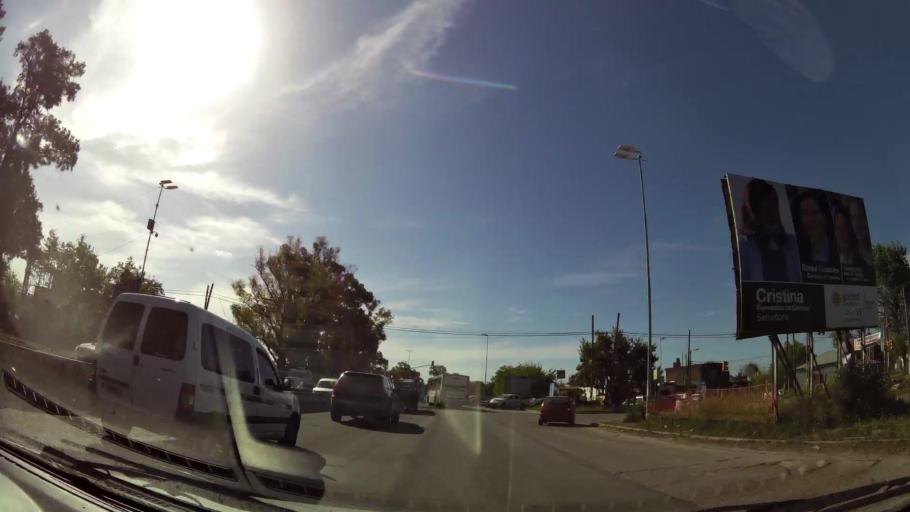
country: AR
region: Buenos Aires
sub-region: Partido de Quilmes
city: Quilmes
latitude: -34.8007
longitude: -58.2386
